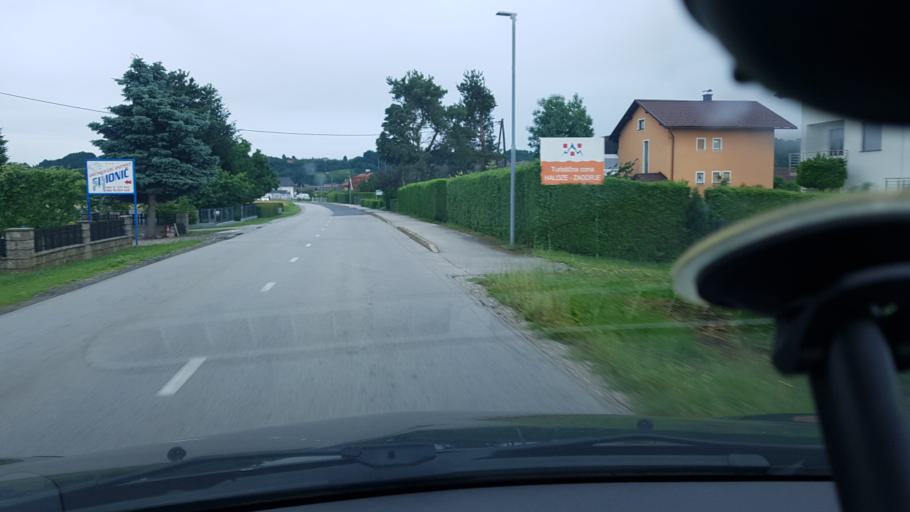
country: SI
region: Videm
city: Videm pri Ptuju
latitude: 46.3745
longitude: 15.8892
